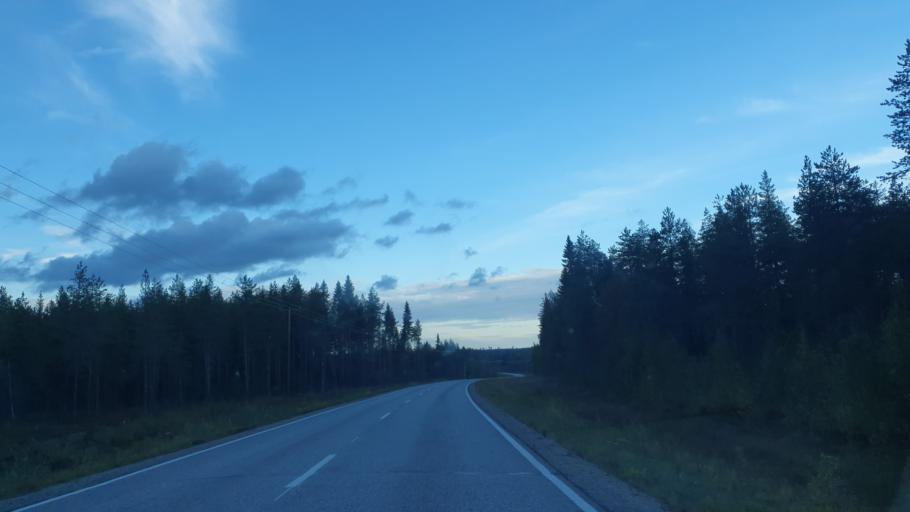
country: FI
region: Kainuu
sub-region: Kehys-Kainuu
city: Kuhmo
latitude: 64.3473
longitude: 29.8767
